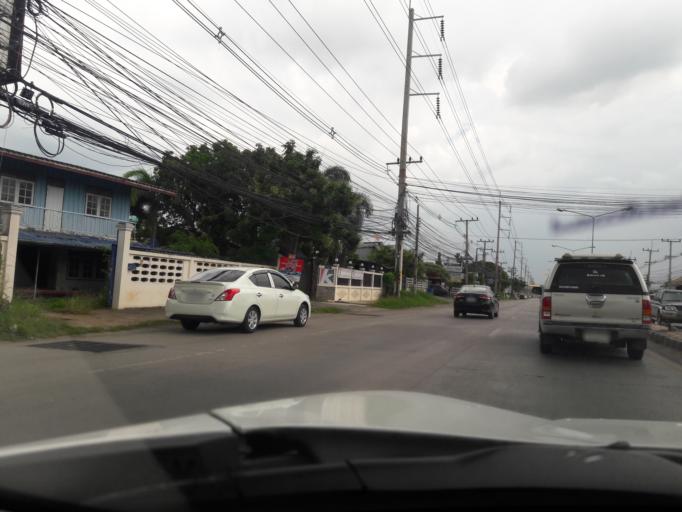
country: TH
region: Lop Buri
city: Lop Buri
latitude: 14.7797
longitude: 100.6896
